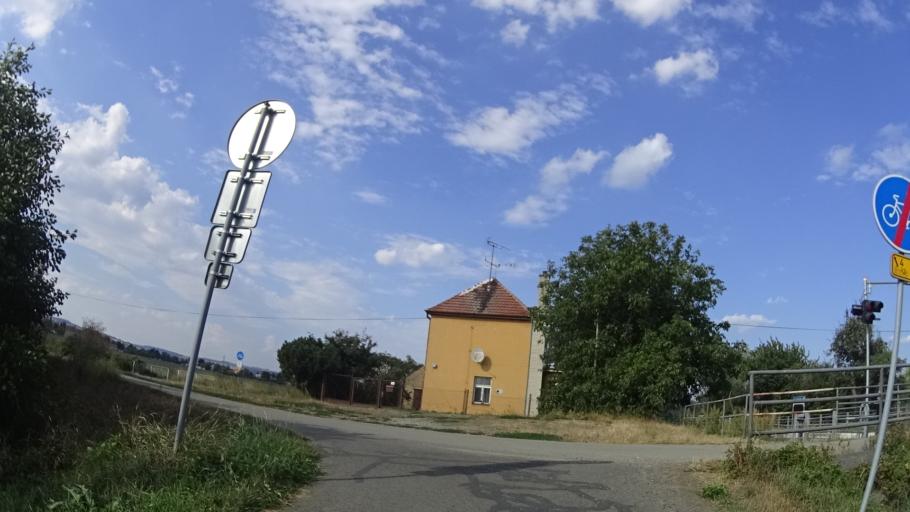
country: CZ
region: Zlin
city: Babice
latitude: 49.1115
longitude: 17.4799
